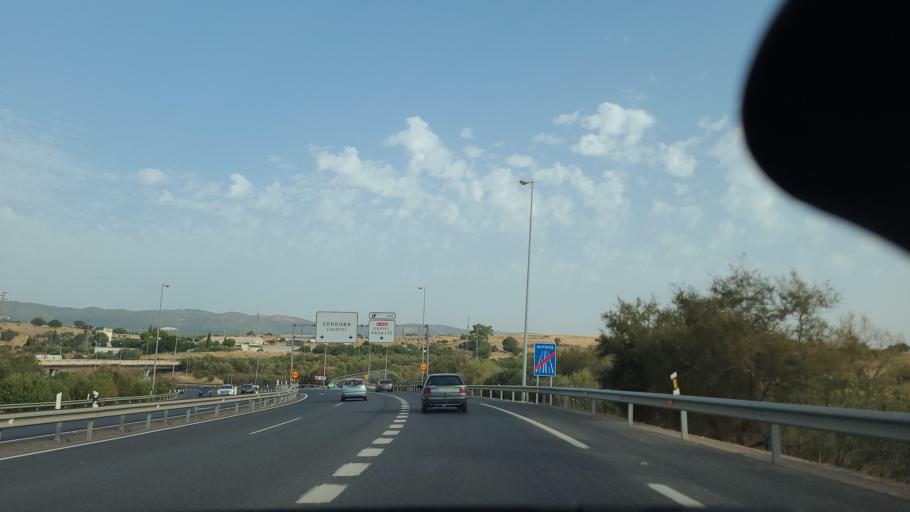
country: ES
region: Andalusia
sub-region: Province of Cordoba
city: Cordoba
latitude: 37.9053
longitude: -4.7516
